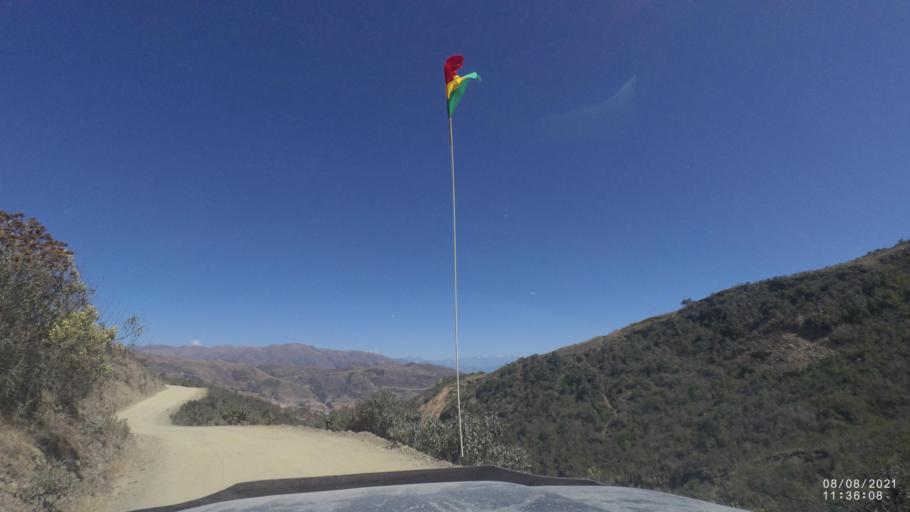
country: BO
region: Cochabamba
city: Colchani
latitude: -16.7795
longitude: -66.6446
